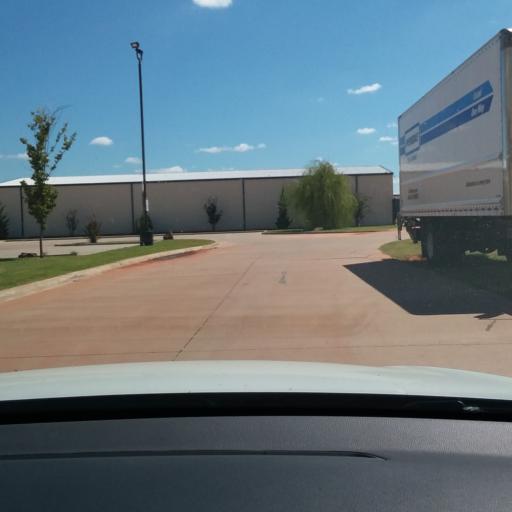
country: US
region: Oklahoma
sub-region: Oklahoma County
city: Edmond
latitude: 35.5902
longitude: -97.4342
